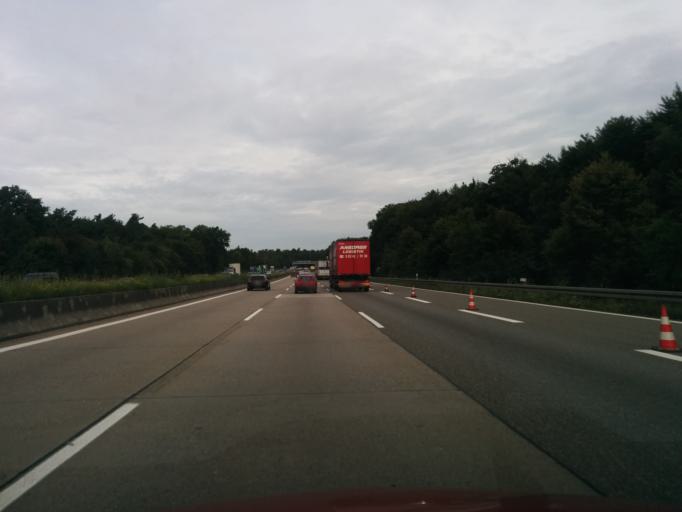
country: DE
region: Baden-Wuerttemberg
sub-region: Regierungsbezirk Stuttgart
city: Sindelfingen
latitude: 48.7318
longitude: 9.0492
